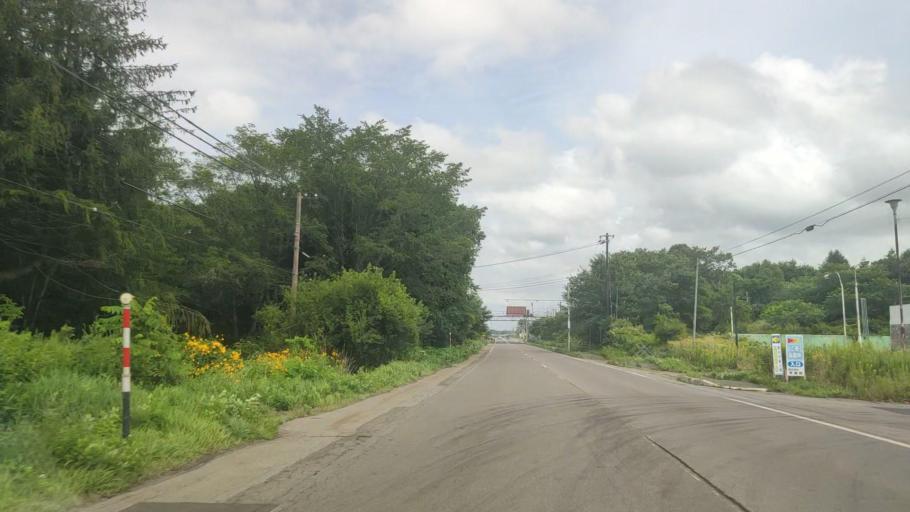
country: JP
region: Hokkaido
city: Nanae
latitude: 41.9984
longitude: 140.6354
